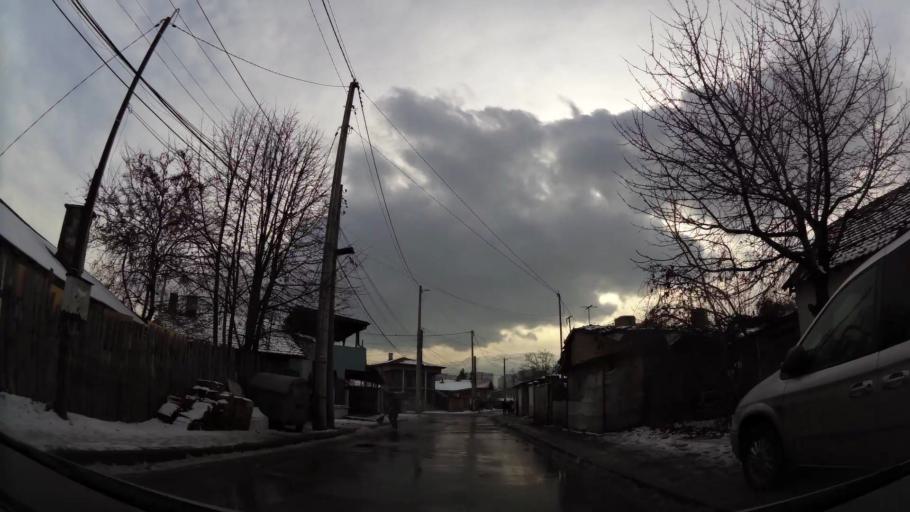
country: BG
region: Sofia-Capital
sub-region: Stolichna Obshtina
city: Sofia
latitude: 42.6893
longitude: 23.3806
